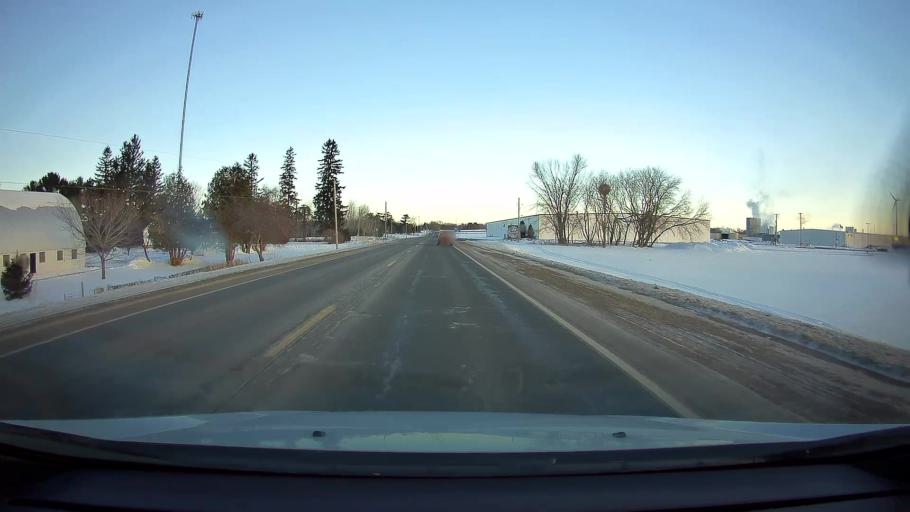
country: US
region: Wisconsin
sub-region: Barron County
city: Turtle Lake
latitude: 45.3872
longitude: -92.1666
